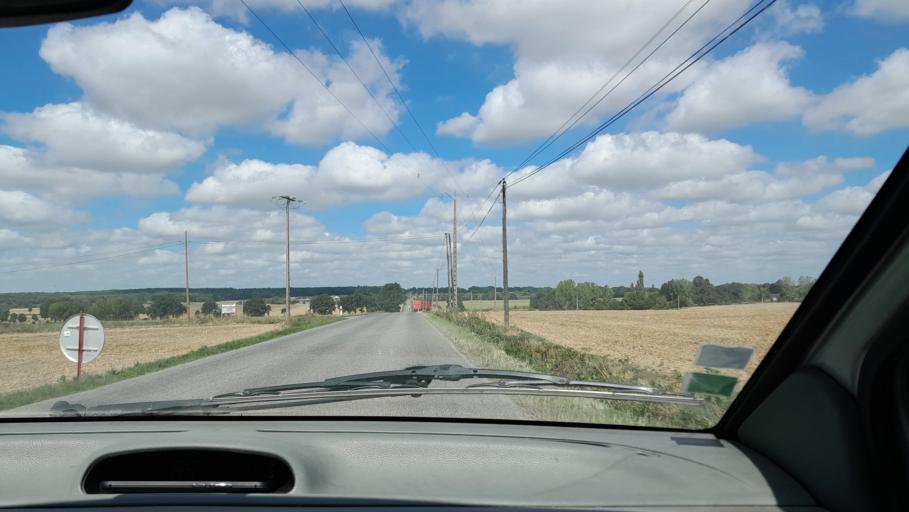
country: FR
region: Pays de la Loire
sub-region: Departement de la Mayenne
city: Ballots
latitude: 47.8719
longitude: -1.0020
